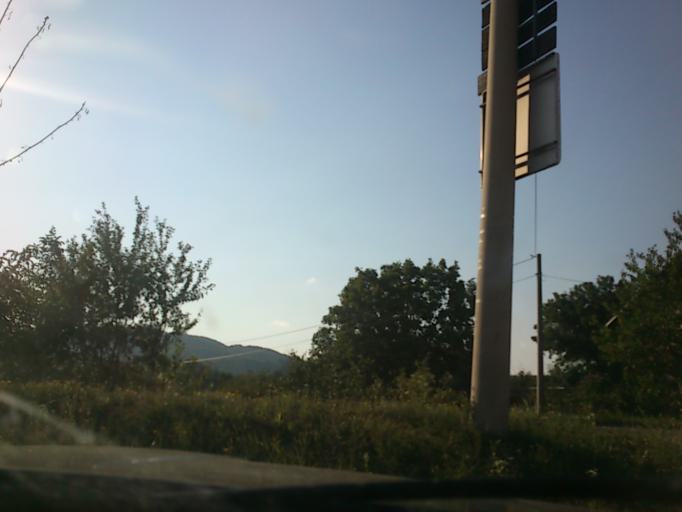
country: HR
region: Licko-Senjska
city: Brinje
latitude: 45.0067
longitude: 15.1403
